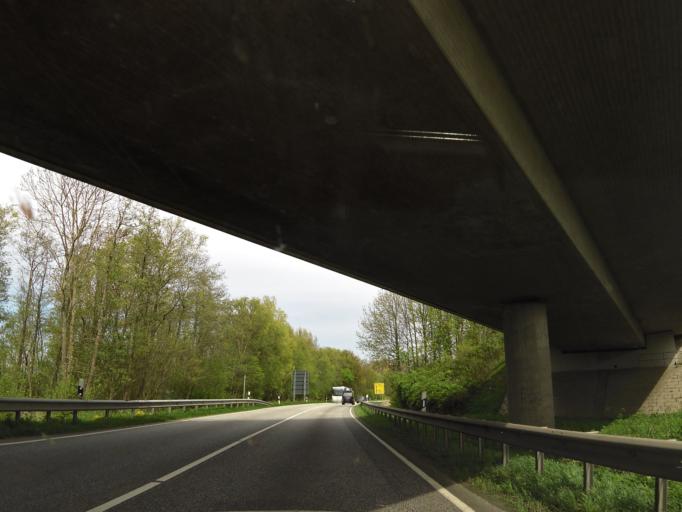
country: DE
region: Schleswig-Holstein
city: Tonning
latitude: 54.3294
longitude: 8.9541
